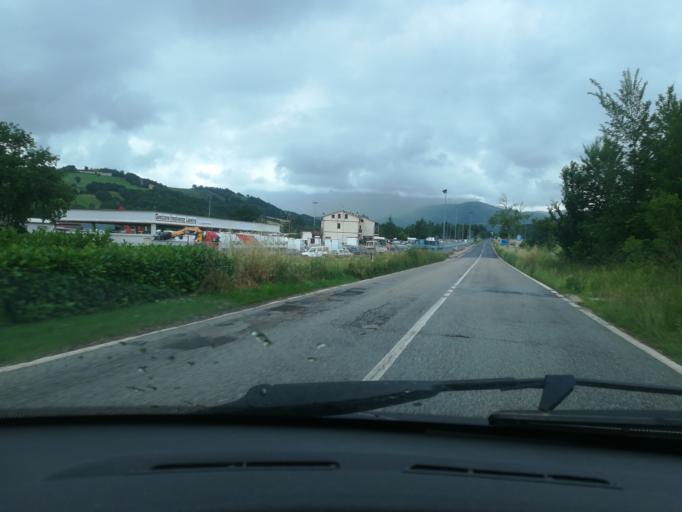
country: IT
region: The Marches
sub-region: Provincia di Macerata
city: San Ginesio
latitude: 43.0909
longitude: 13.3149
